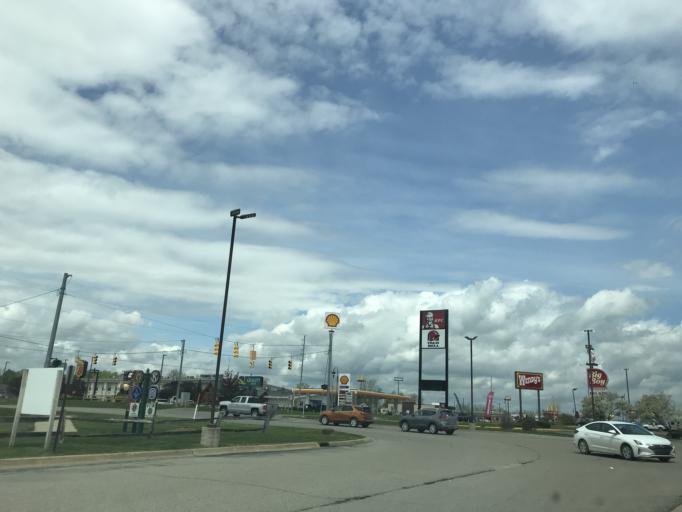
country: US
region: Michigan
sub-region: Ogemaw County
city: West Branch
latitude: 44.2485
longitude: -84.2249
